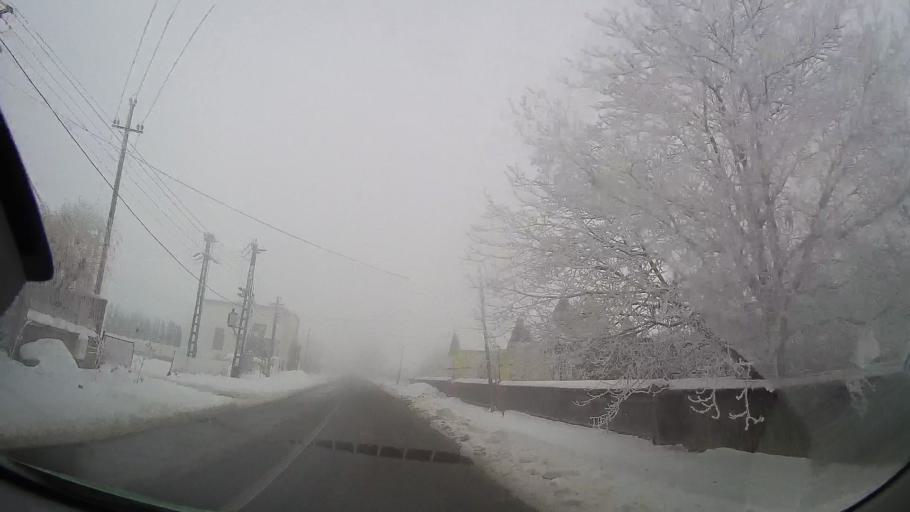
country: RO
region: Neamt
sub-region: Comuna Sabaoani
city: Sabaoani
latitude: 47.0243
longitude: 26.8626
